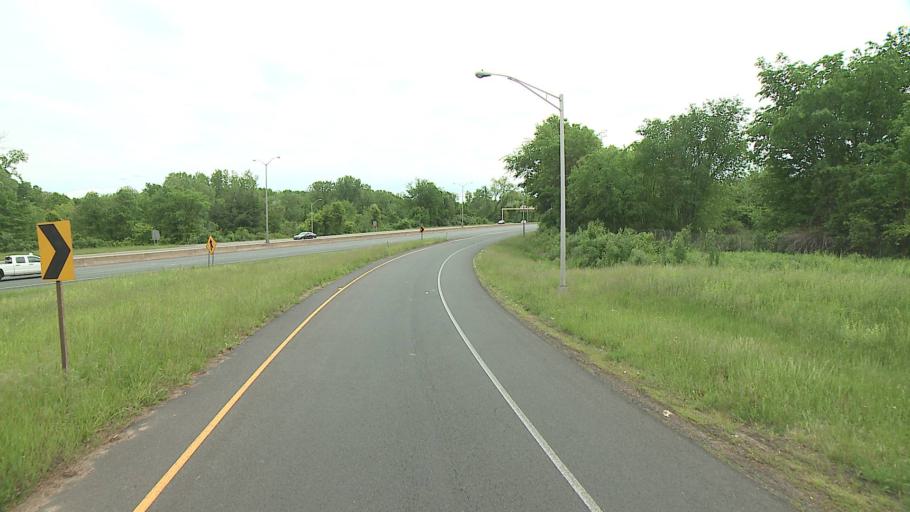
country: US
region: Connecticut
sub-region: Hartford County
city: Enfield
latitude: 41.9876
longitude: -72.5890
